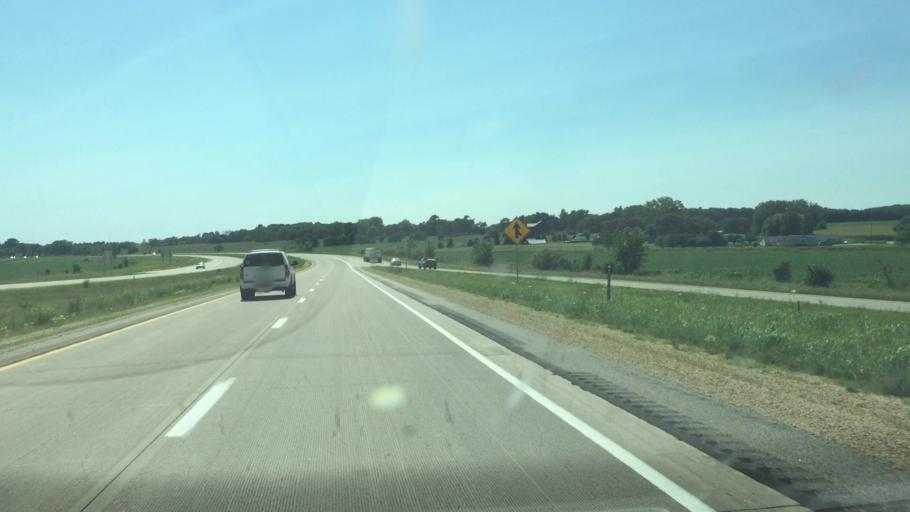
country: US
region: Iowa
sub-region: Jones County
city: Monticello
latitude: 42.2072
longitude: -91.1928
